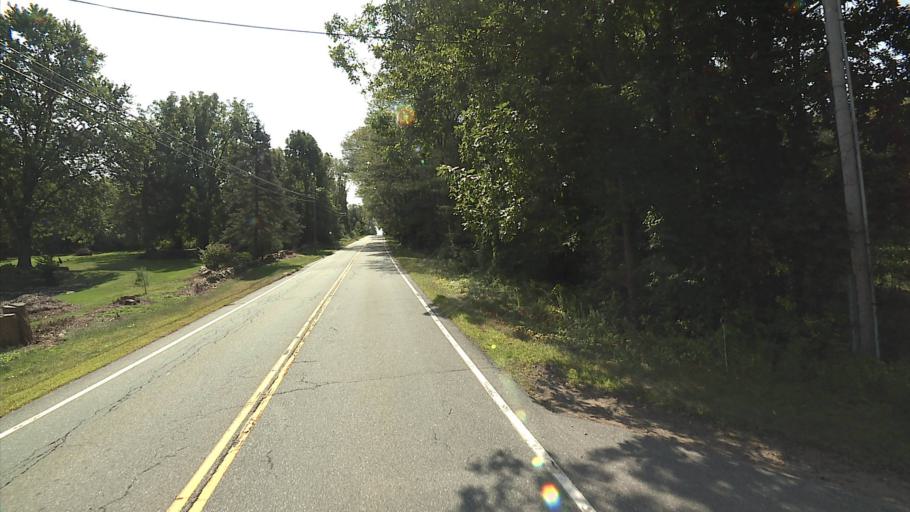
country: US
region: Connecticut
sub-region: Windham County
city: South Woodstock
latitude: 41.9747
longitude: -71.9912
